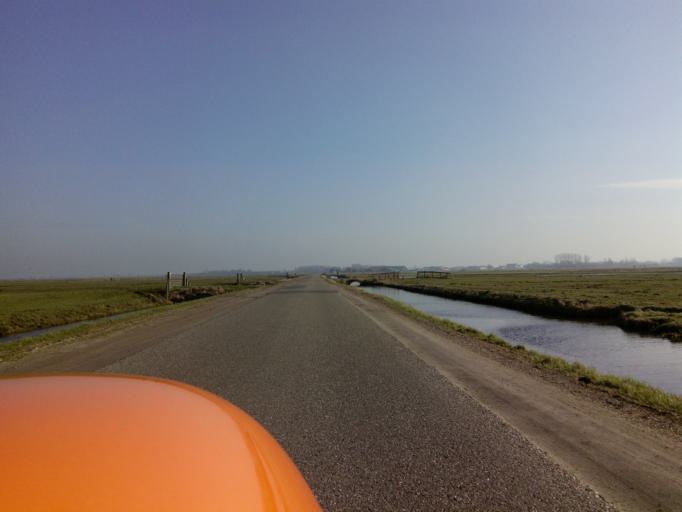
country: NL
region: Utrecht
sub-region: Gemeente Bunschoten
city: Bunschoten
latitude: 52.2343
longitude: 5.4323
